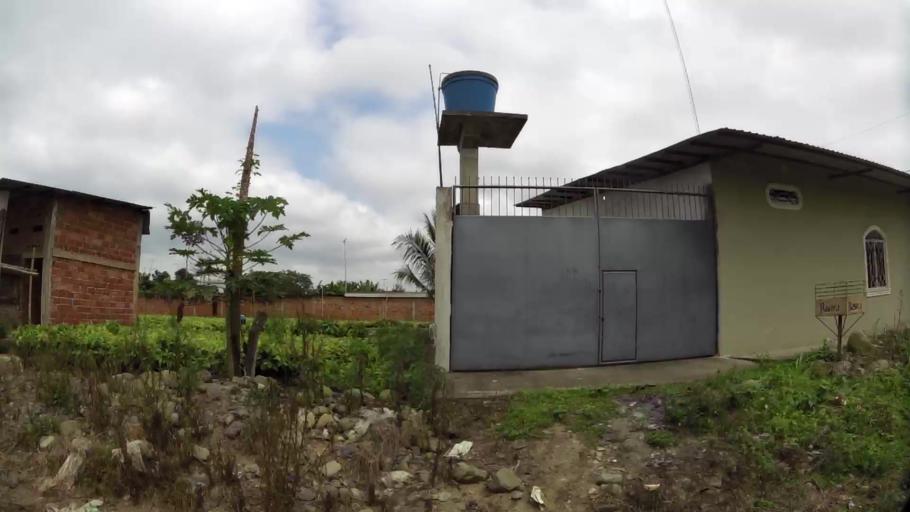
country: EC
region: Guayas
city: Naranjal
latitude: -2.6837
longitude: -79.6212
